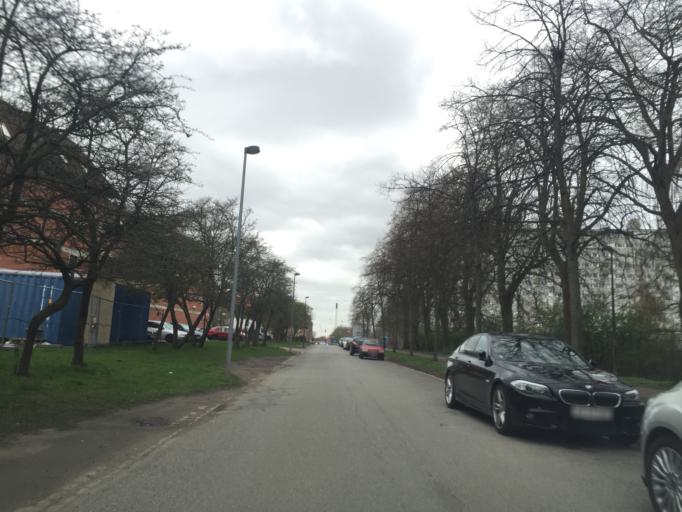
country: DK
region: Capital Region
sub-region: Kobenhavn
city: Copenhagen
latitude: 55.7140
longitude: 12.5628
